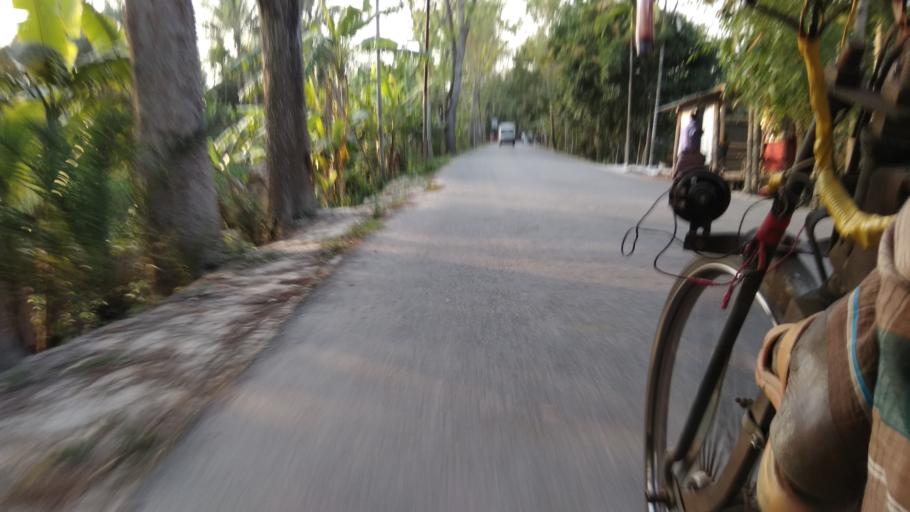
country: BD
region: Barisal
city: Mehendiganj
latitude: 22.9223
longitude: 90.4070
